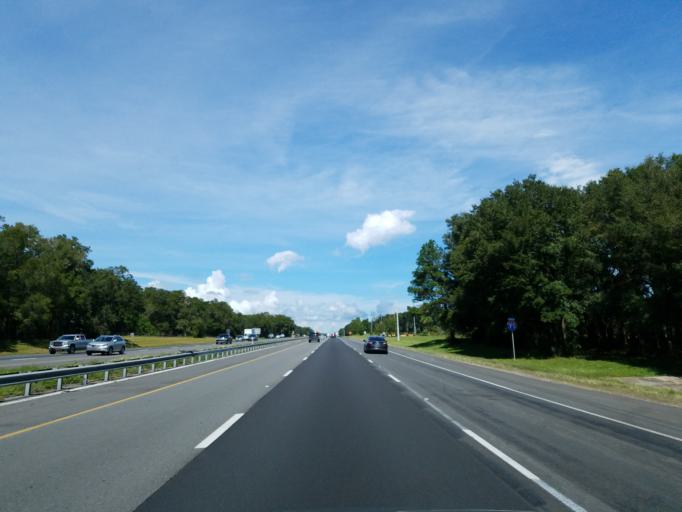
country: US
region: Florida
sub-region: Marion County
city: Ocala
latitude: 29.2734
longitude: -82.1953
